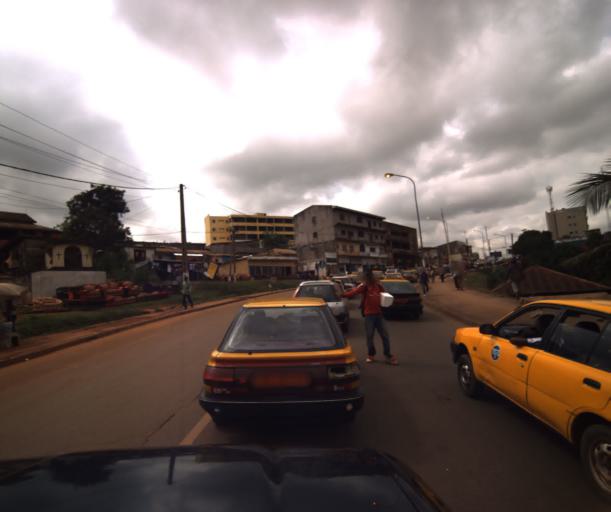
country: CM
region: Centre
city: Yaounde
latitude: 3.8535
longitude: 11.5223
